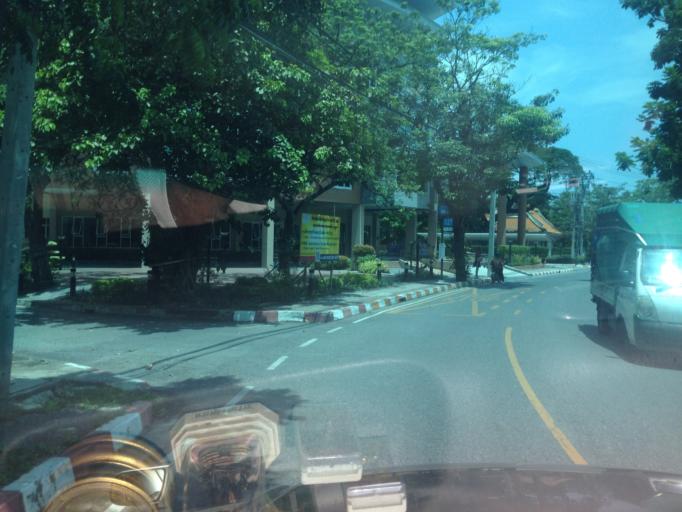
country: TH
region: Chon Buri
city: Si Racha
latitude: 13.2732
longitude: 100.9284
